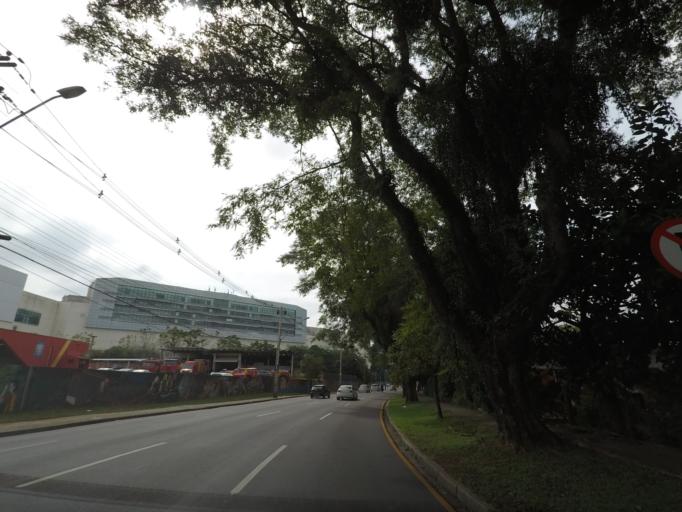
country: BR
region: Parana
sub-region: Curitiba
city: Curitiba
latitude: -25.4799
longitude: -49.2907
